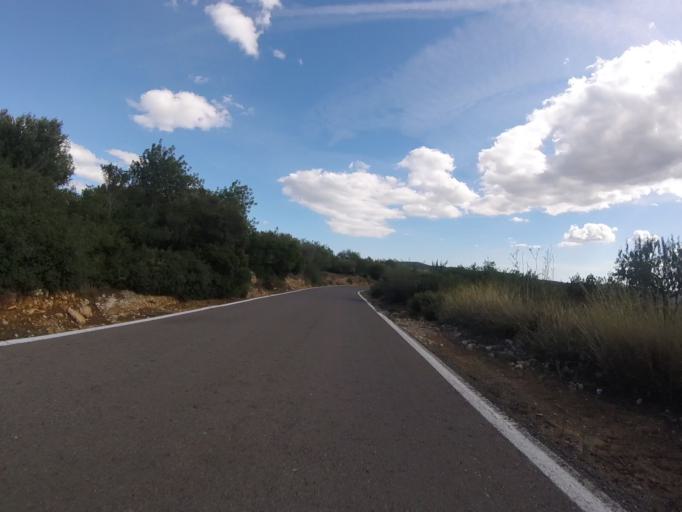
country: ES
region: Valencia
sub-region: Provincia de Castello
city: Cuevas de Vinroma
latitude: 40.3737
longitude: 0.1139
